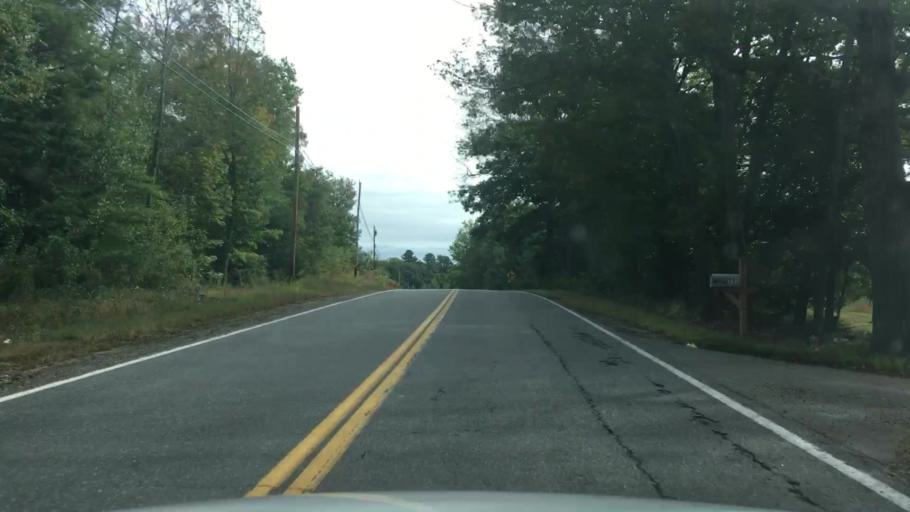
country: US
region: Maine
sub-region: Sagadahoc County
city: Topsham
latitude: 43.9444
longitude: -70.0282
